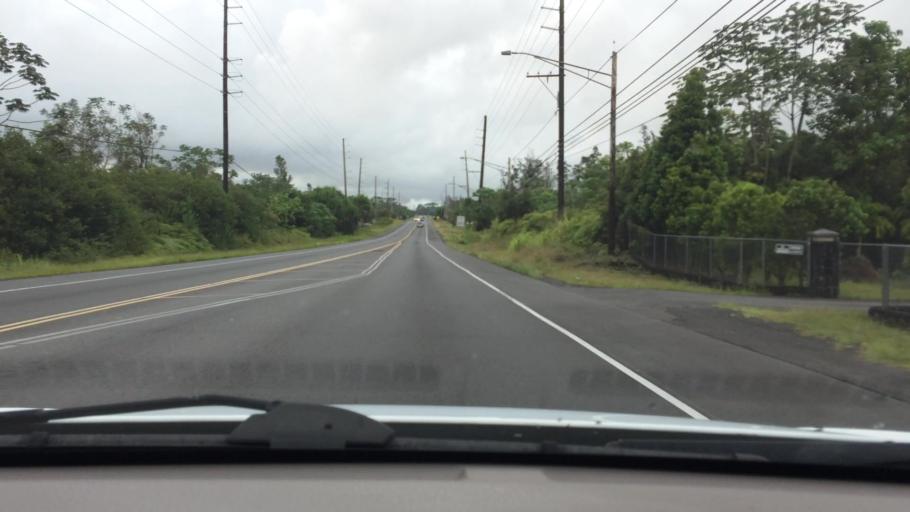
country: US
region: Hawaii
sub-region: Hawaii County
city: Orchidlands Estates
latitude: 19.5696
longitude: -154.9993
